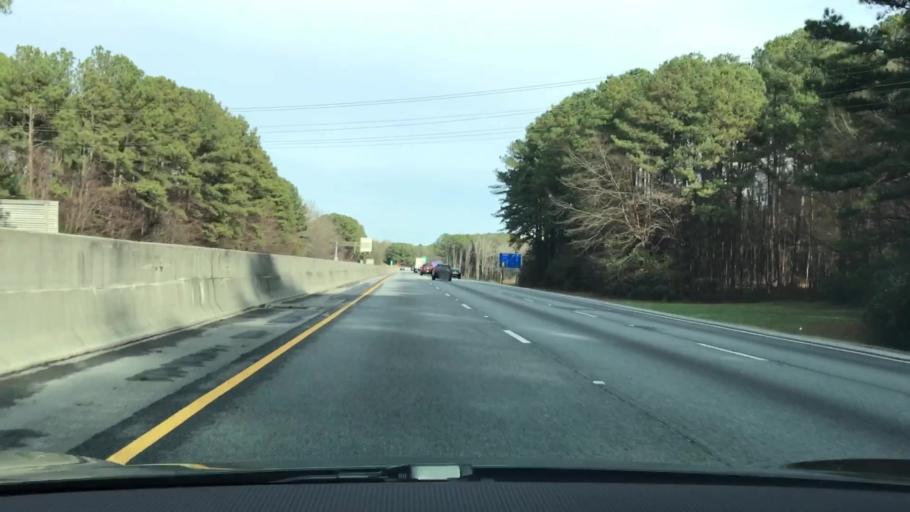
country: US
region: Georgia
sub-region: Newton County
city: Oxford
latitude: 33.6114
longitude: -83.8648
